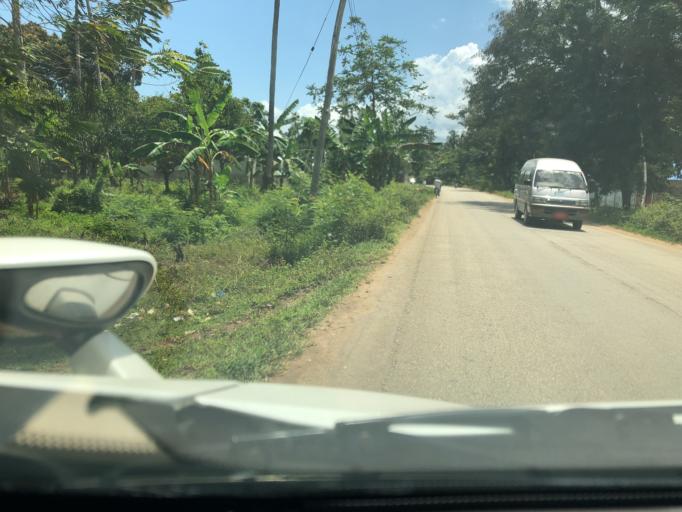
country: TZ
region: Zanzibar Central/South
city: Koani
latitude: -6.0648
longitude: 39.2518
